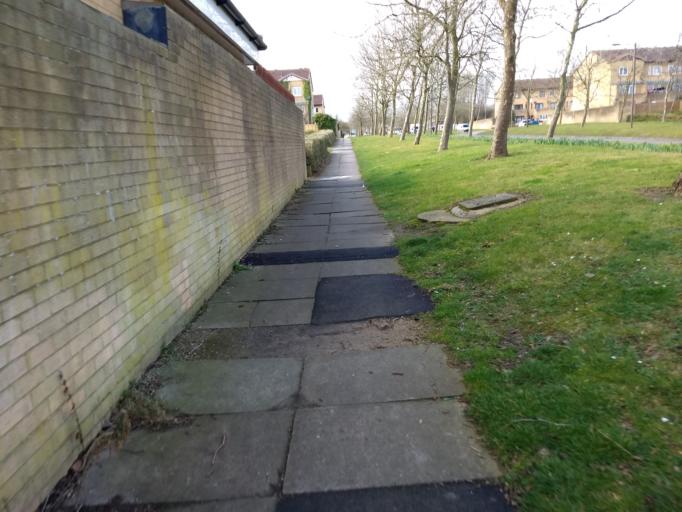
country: GB
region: England
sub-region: Milton Keynes
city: Milton Keynes
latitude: 52.0351
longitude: -0.7423
